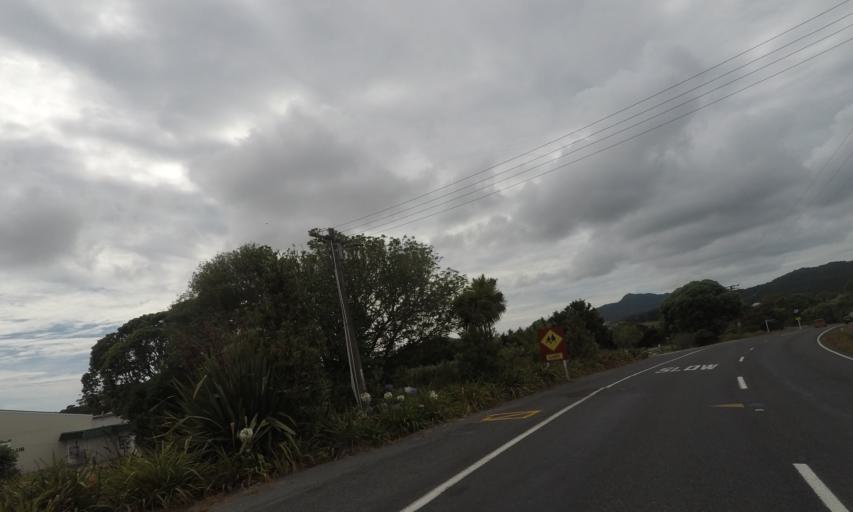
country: NZ
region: Northland
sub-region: Whangarei
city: Ruakaka
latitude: -35.7679
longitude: 174.4769
